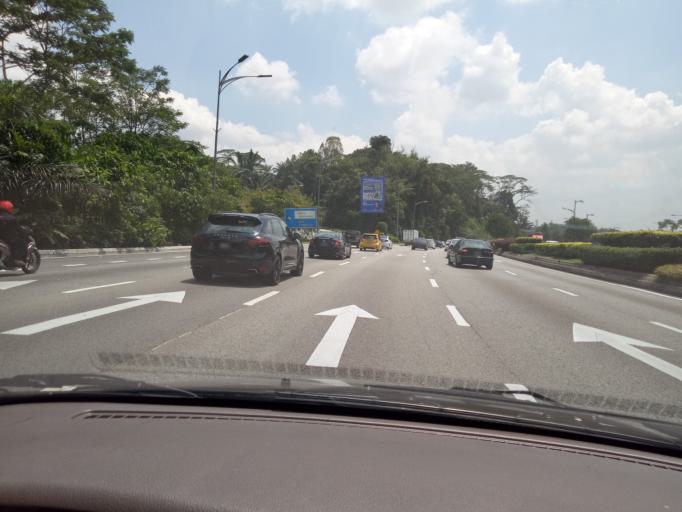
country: MY
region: Kuala Lumpur
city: Kuala Lumpur
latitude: 3.1421
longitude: 101.6791
